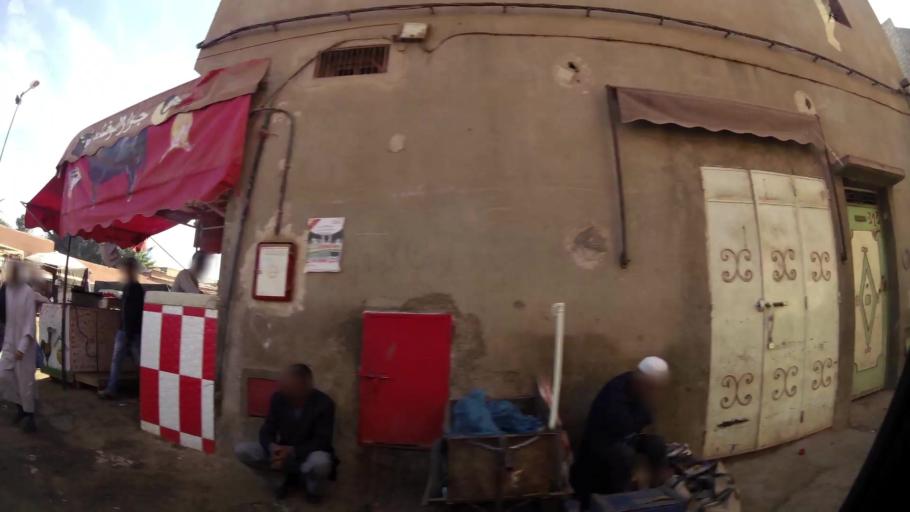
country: MA
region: Marrakech-Tensift-Al Haouz
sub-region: Marrakech
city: Marrakesh
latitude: 31.6090
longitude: -7.9624
